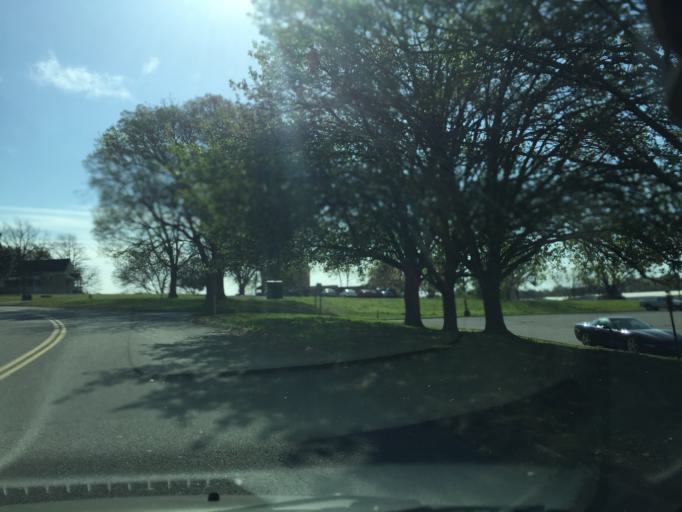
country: US
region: Tennessee
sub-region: Hamilton County
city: Harrison
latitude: 35.0722
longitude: -85.1848
